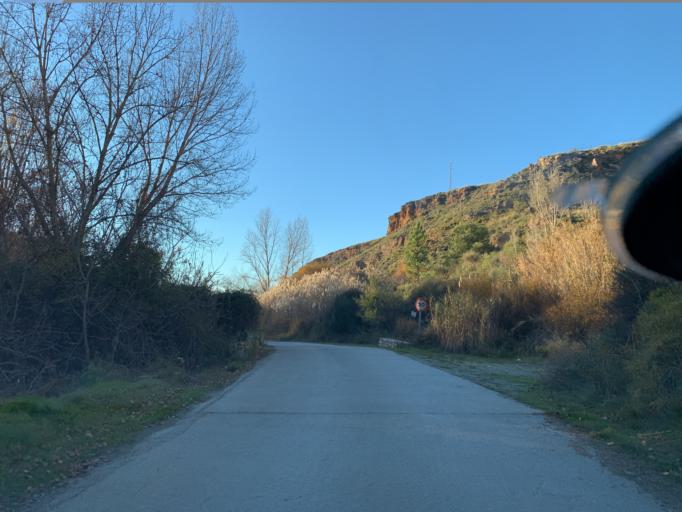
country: ES
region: Andalusia
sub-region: Provincia de Granada
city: Dilar
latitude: 37.0638
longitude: -3.5593
